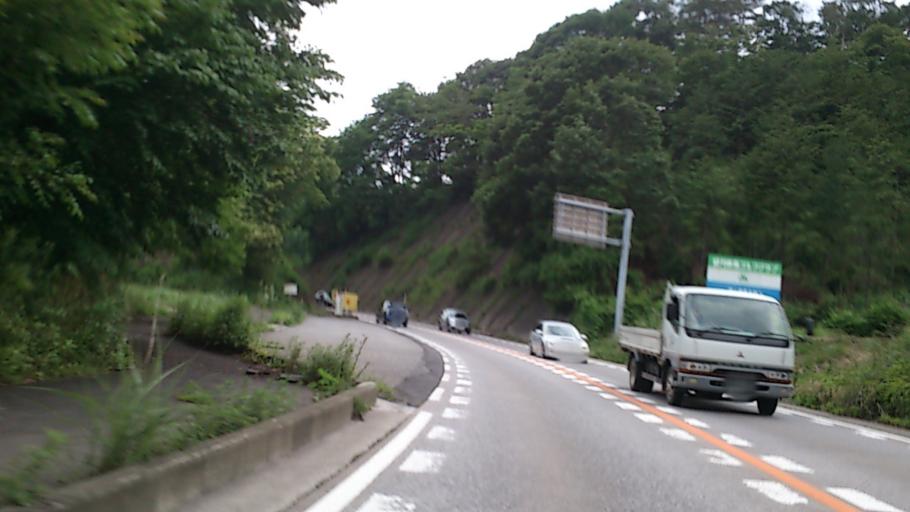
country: JP
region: Nagano
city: Komoro
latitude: 36.2660
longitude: 138.3728
